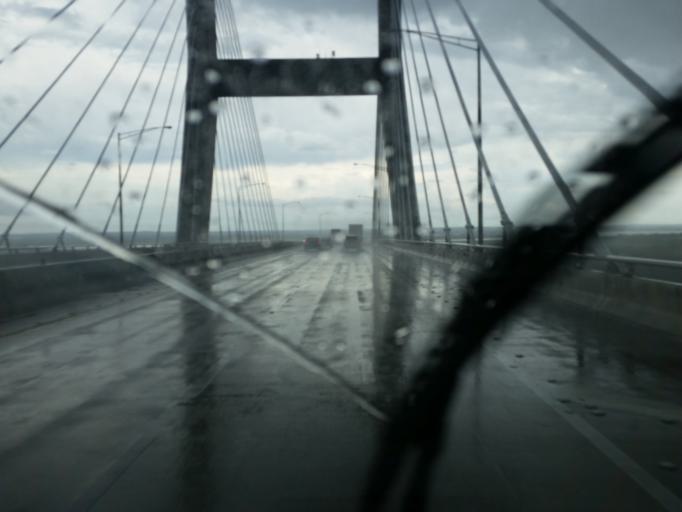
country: US
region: Alabama
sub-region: Mobile County
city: Prichard
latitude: 30.7334
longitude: -88.0427
